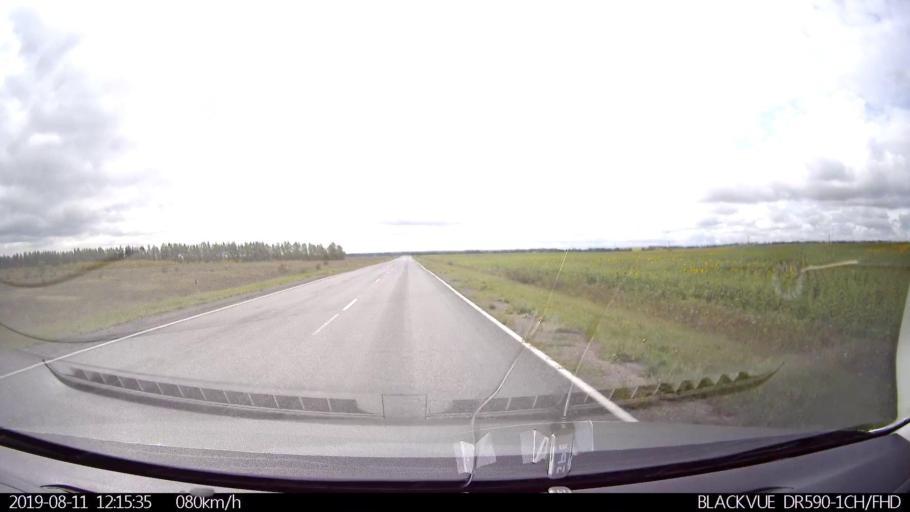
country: RU
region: Ulyanovsk
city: Ignatovka
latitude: 53.9402
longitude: 47.9674
